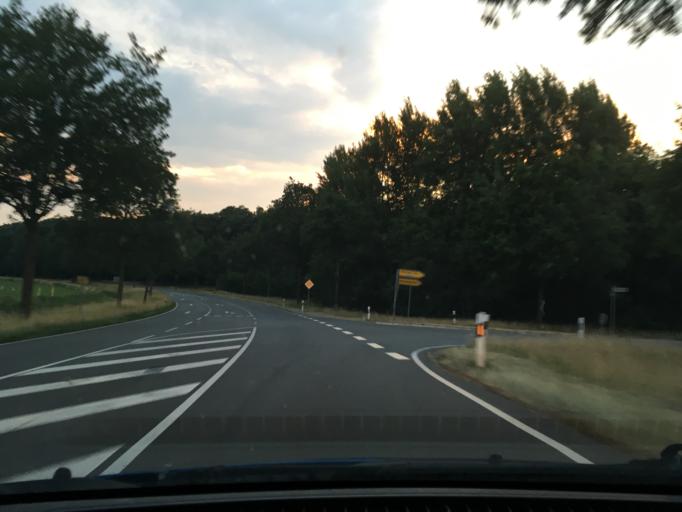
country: DE
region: Lower Saxony
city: Bad Bevensen
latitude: 53.0797
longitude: 10.5589
